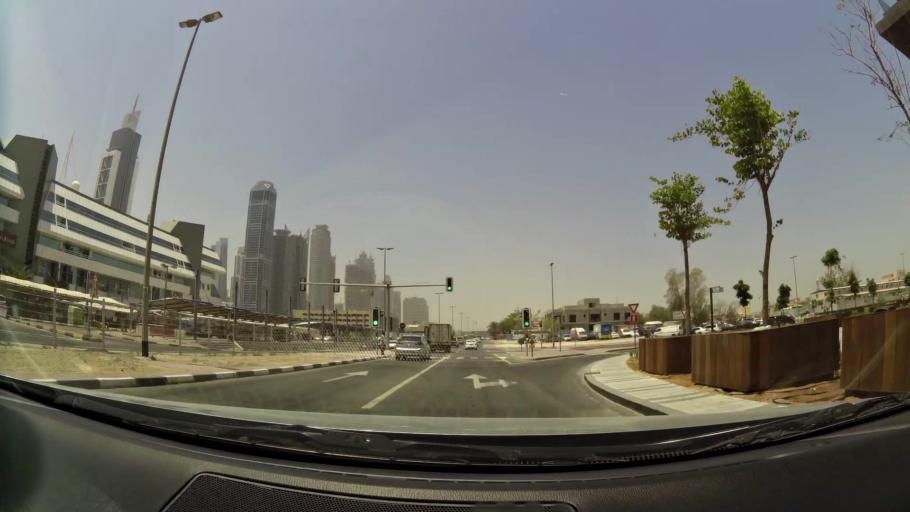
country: AE
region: Dubai
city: Dubai
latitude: 25.1997
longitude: 55.2647
